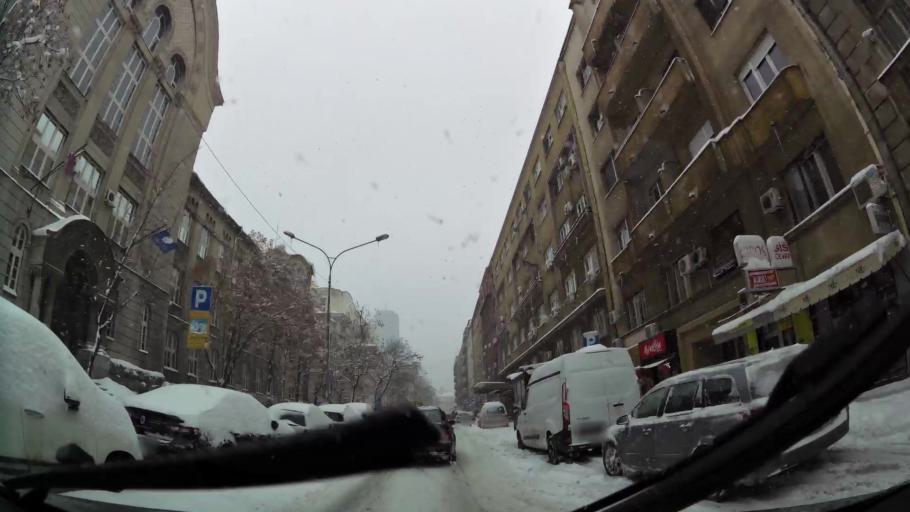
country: RS
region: Central Serbia
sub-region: Belgrade
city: Stari Grad
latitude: 44.8102
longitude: 20.4601
